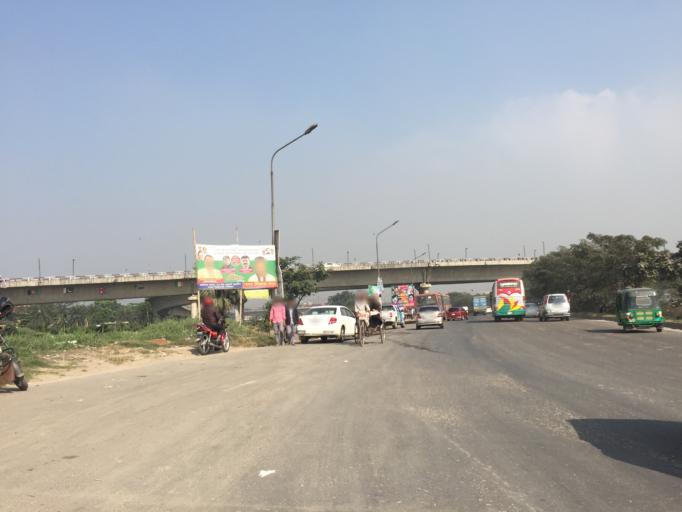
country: BD
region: Dhaka
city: Tungi
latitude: 23.8214
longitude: 90.4196
